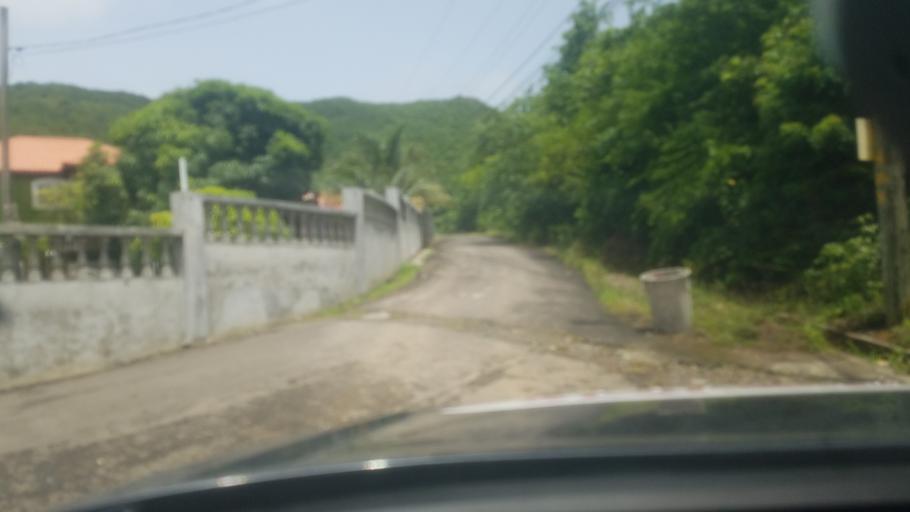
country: LC
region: Gros-Islet
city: Gros Islet
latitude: 14.0512
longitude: -60.9356
